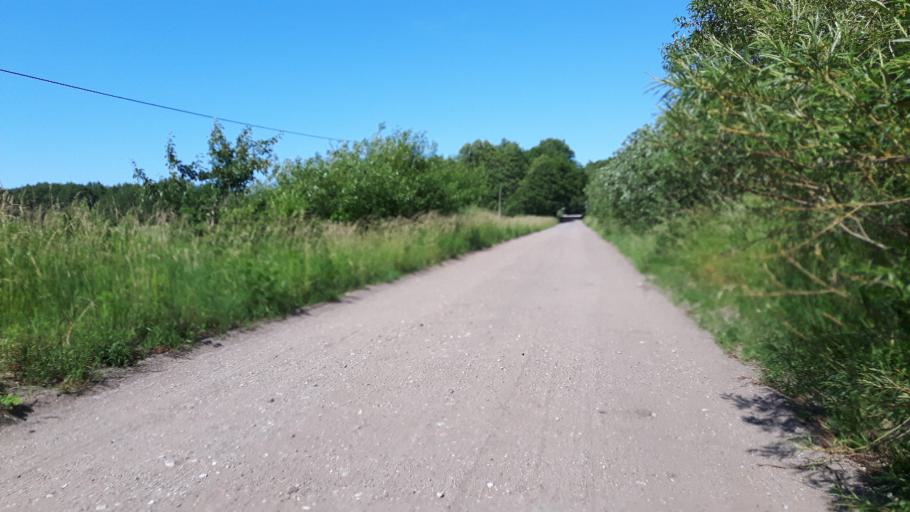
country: PL
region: Pomeranian Voivodeship
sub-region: Powiat slupski
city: Glowczyce
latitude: 54.6908
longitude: 17.4464
